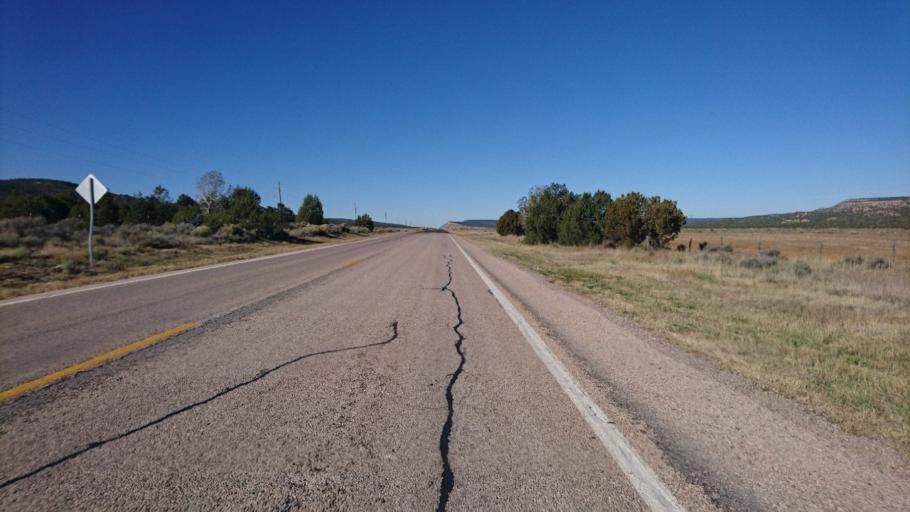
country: US
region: New Mexico
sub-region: McKinley County
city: Black Rock
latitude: 35.1217
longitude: -108.6387
